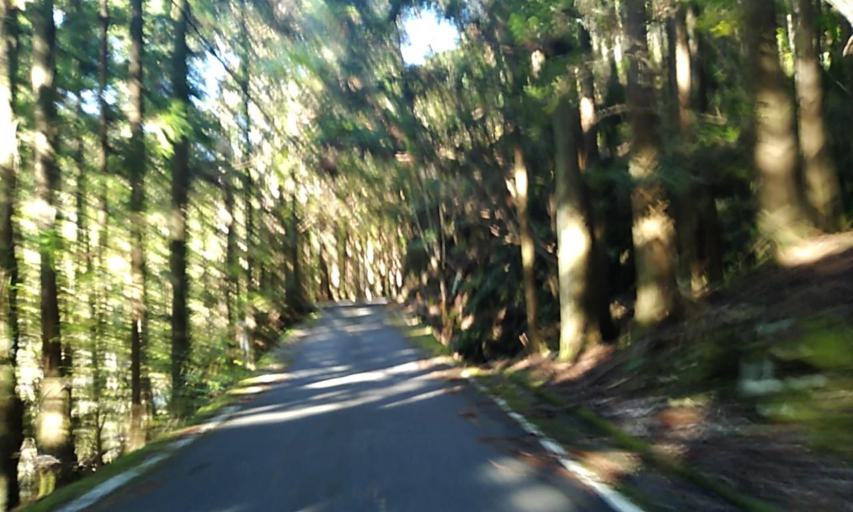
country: JP
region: Wakayama
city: Shingu
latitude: 33.9082
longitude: 136.0006
